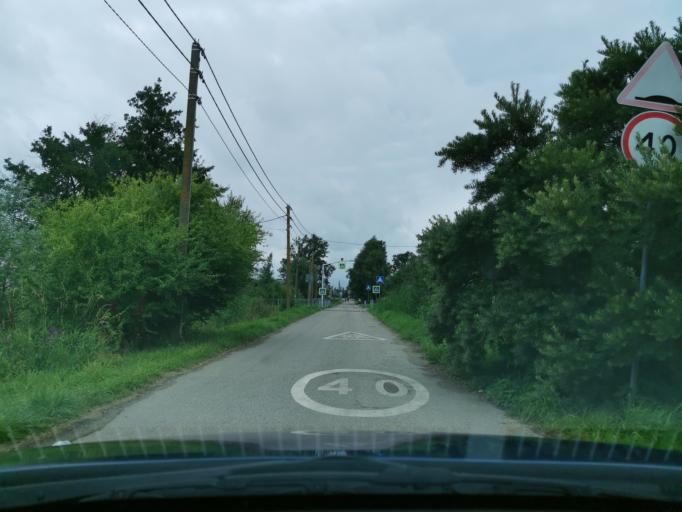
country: LT
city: Nida
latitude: 55.1519
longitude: 20.8513
